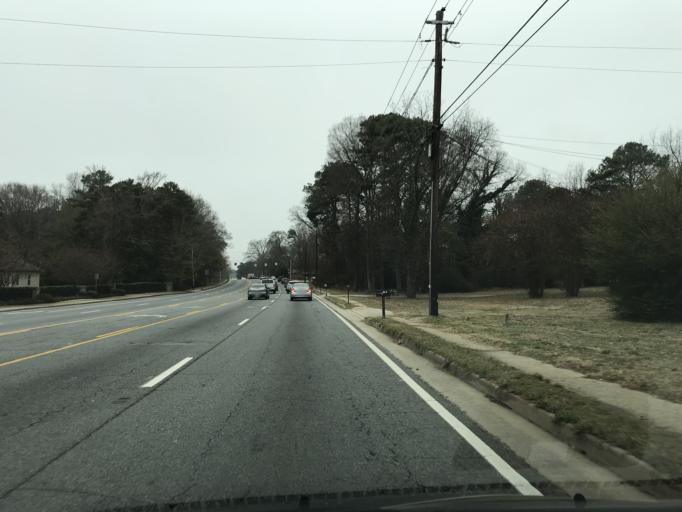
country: US
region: Georgia
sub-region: DeKalb County
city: Clarkston
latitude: 33.8364
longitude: -84.2401
